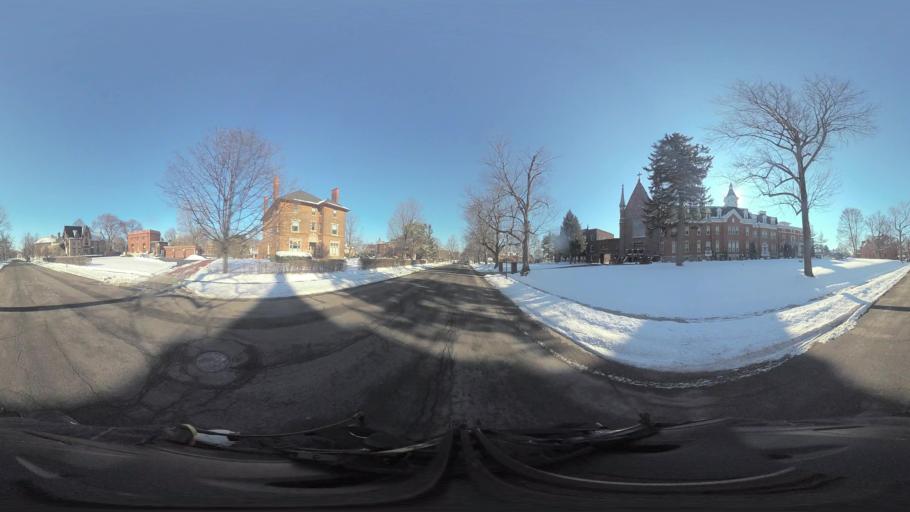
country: US
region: New York
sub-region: Monroe County
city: Rochester
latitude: 43.1562
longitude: -77.5913
